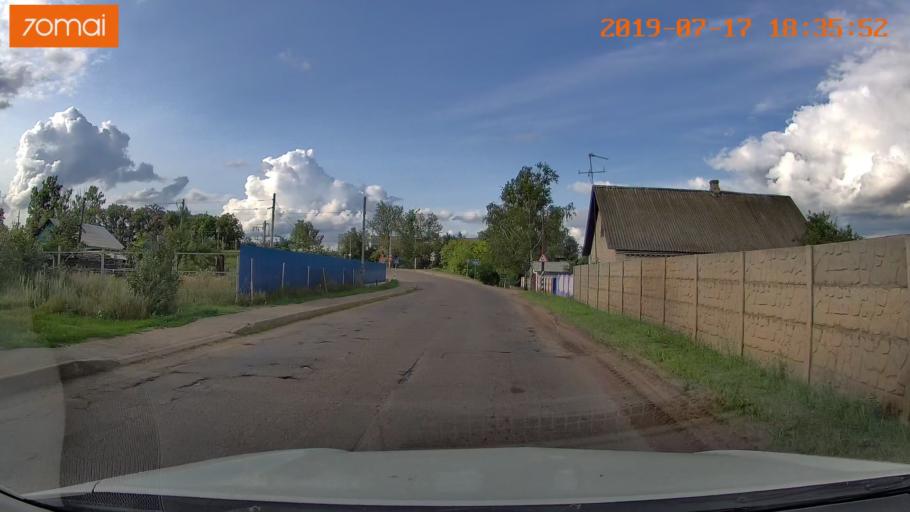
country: BY
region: Mogilev
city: Asipovichy
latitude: 53.2958
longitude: 28.6601
